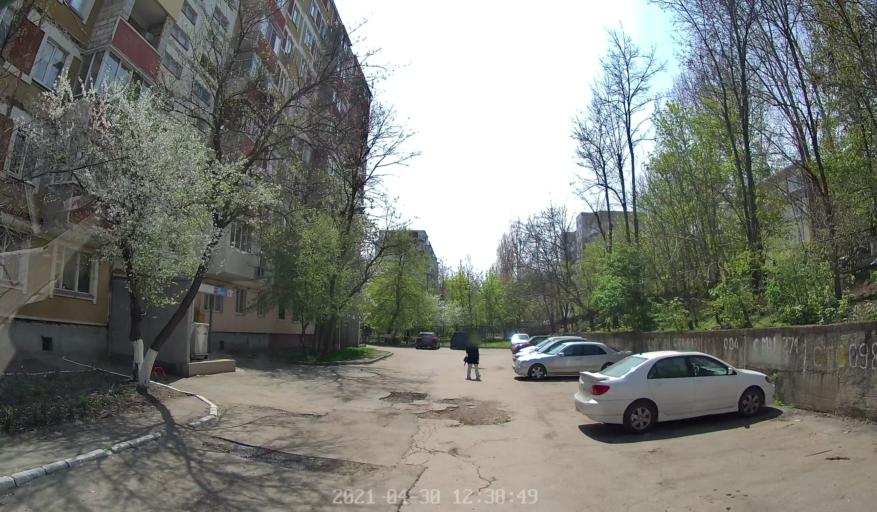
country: MD
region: Chisinau
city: Stauceni
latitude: 47.0535
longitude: 28.8948
